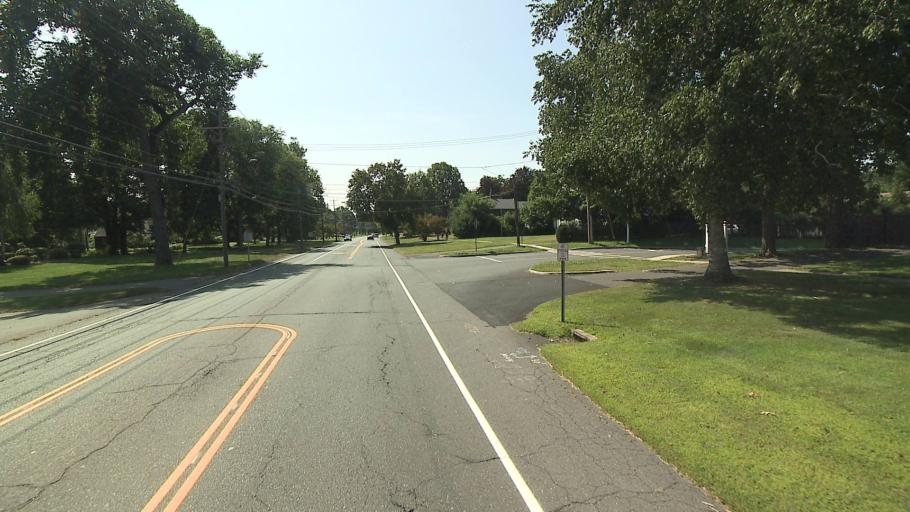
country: US
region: Connecticut
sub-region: Hartford County
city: Enfield
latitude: 41.9794
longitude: -72.5923
